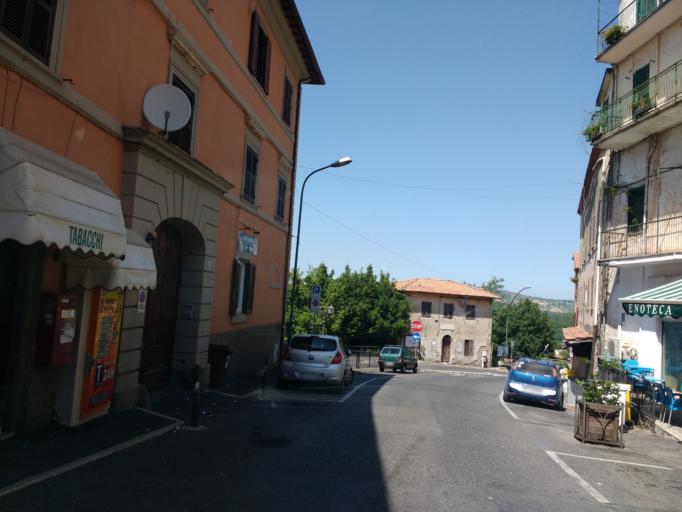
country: IT
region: Latium
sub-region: Citta metropolitana di Roma Capitale
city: Rocca di Papa
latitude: 41.7622
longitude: 12.7070
